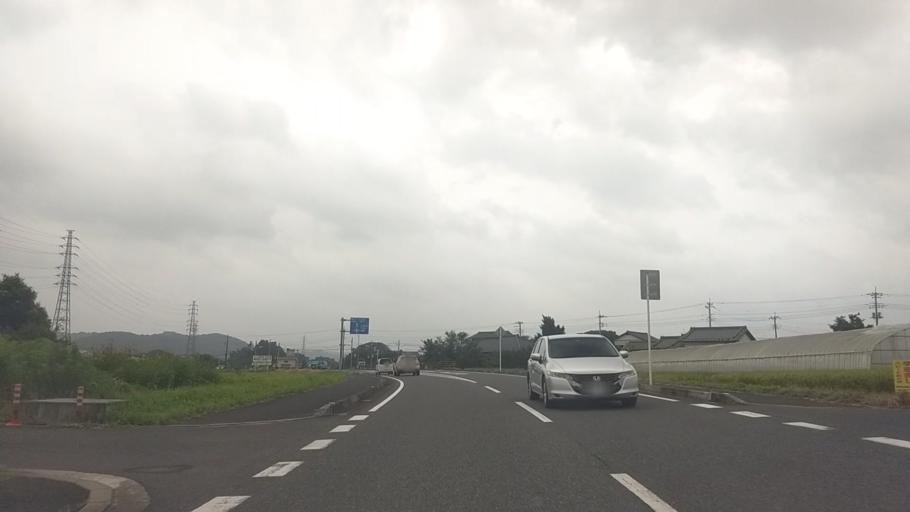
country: JP
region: Chiba
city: Kisarazu
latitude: 35.3149
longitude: 140.0550
